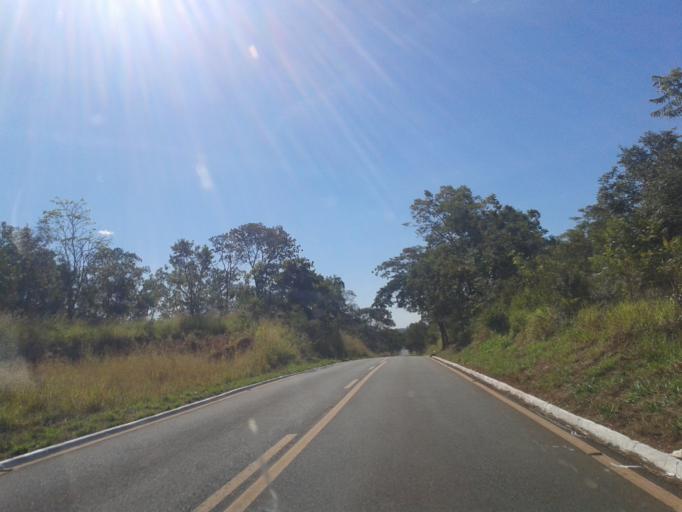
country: BR
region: Minas Gerais
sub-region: Ituiutaba
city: Ituiutaba
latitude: -19.1834
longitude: -49.7810
